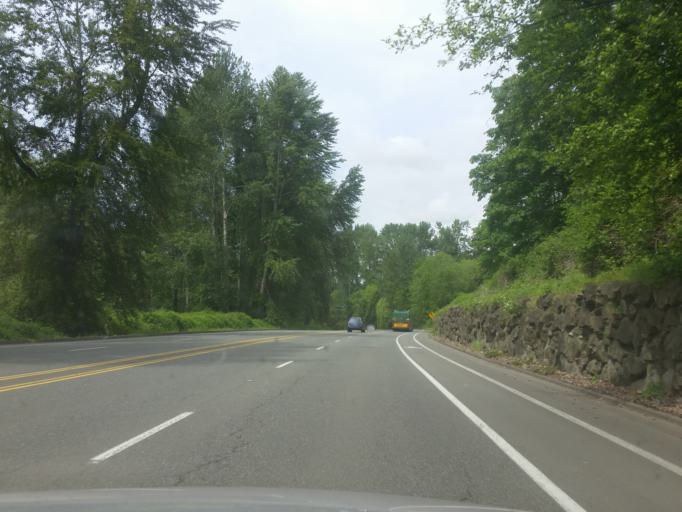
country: US
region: Washington
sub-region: King County
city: Kirkland
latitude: 47.6993
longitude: -122.2084
